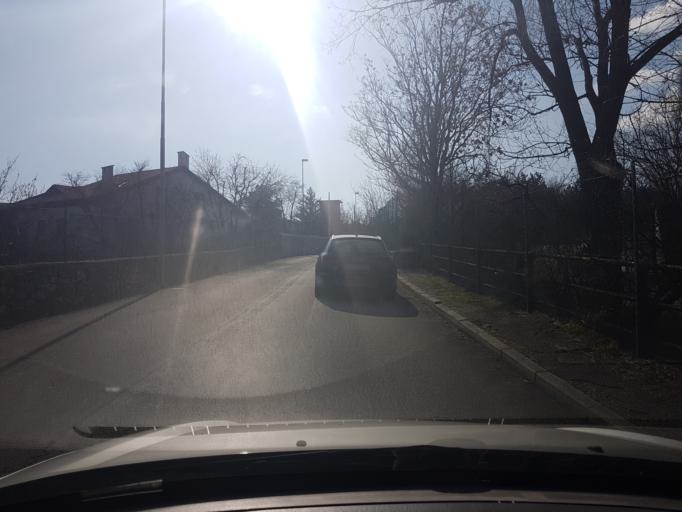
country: IT
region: Friuli Venezia Giulia
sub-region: Provincia di Trieste
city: Aurisina Cave
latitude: 45.7555
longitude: 13.6586
